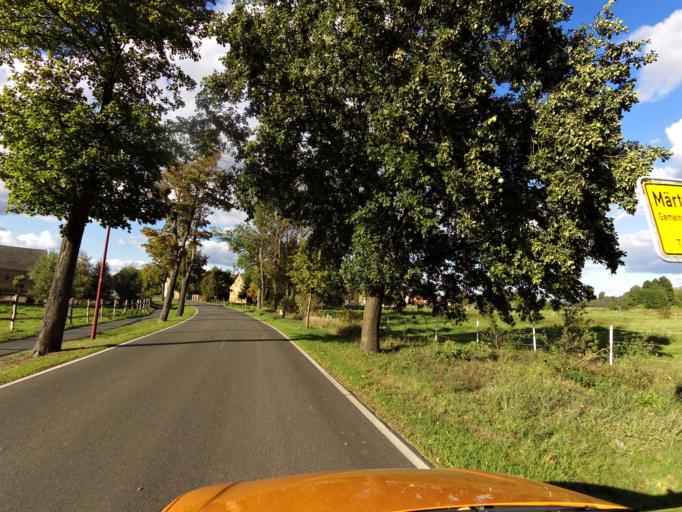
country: DE
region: Brandenburg
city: Trebbin
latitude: 52.1599
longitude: 13.1847
